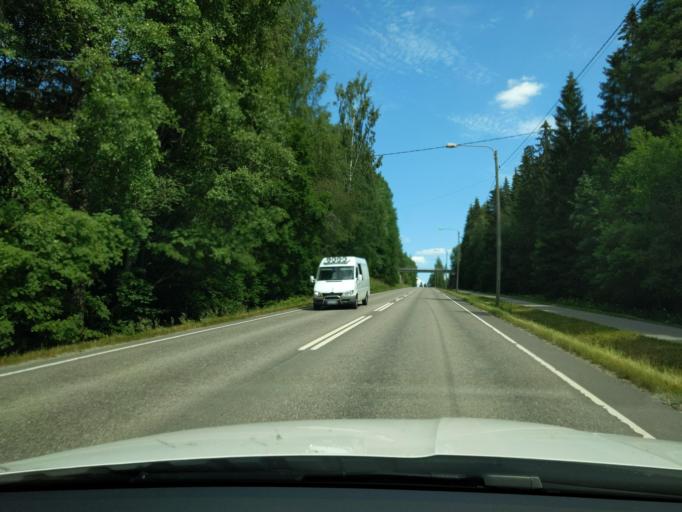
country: FI
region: Paijanne Tavastia
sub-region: Lahti
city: Lahti
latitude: 61.0139
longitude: 25.7091
